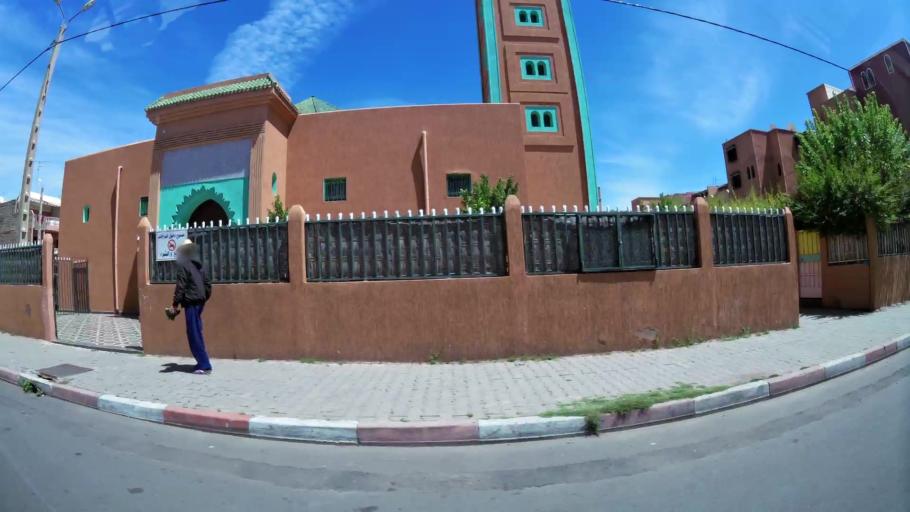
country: MA
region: Marrakech-Tensift-Al Haouz
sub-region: Marrakech
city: Marrakesh
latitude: 31.6398
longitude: -8.0526
